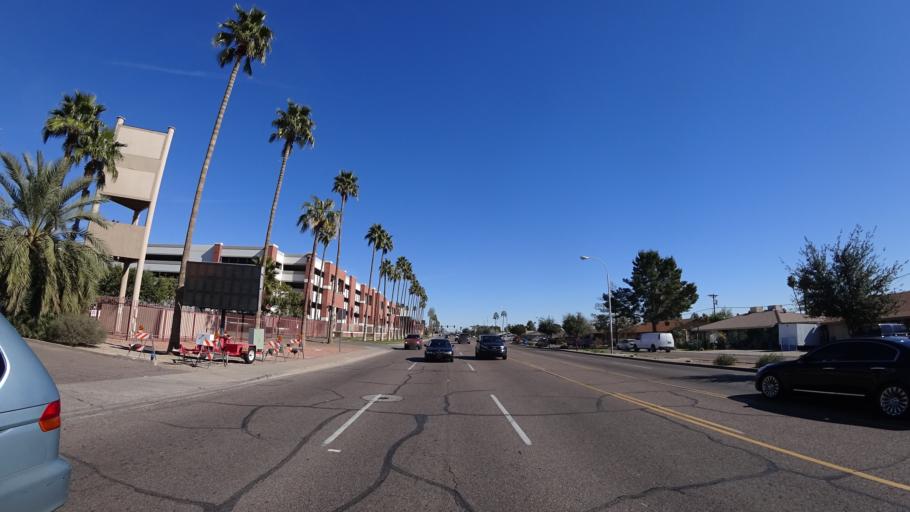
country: US
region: Arizona
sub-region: Maricopa County
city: Glendale
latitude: 33.5095
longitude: -112.1321
